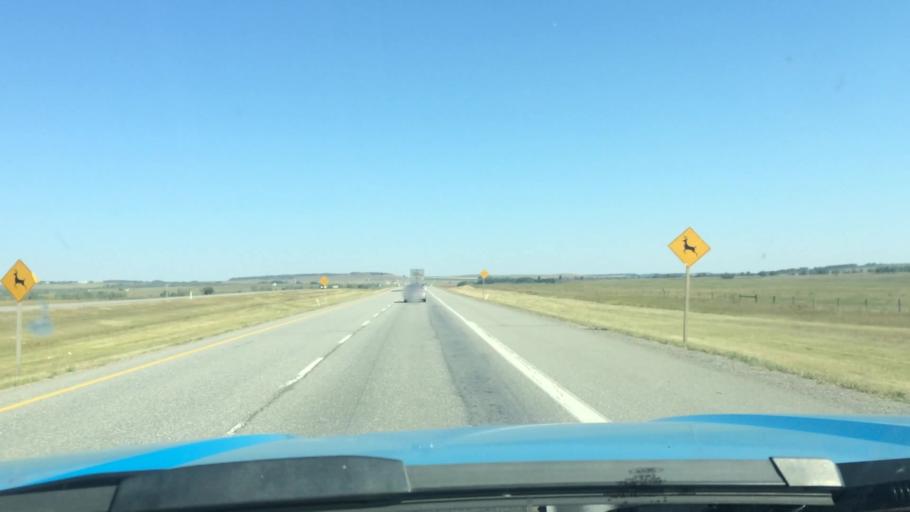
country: CA
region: Alberta
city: Cochrane
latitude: 51.0874
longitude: -114.5290
